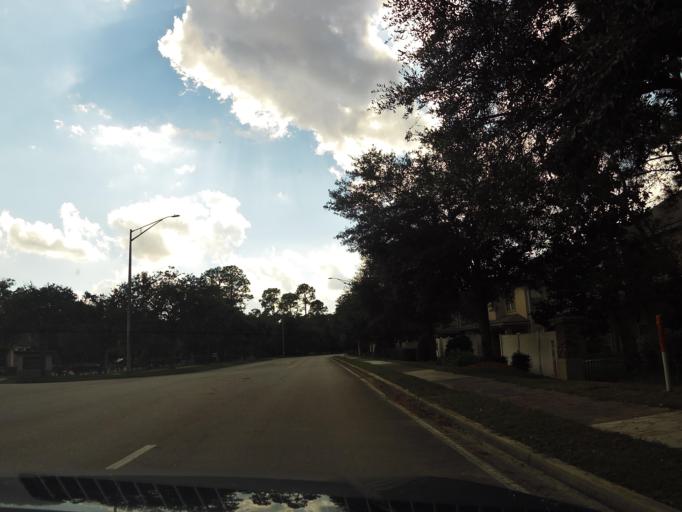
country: US
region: Florida
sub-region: Duval County
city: Jacksonville
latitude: 30.2425
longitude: -81.5947
